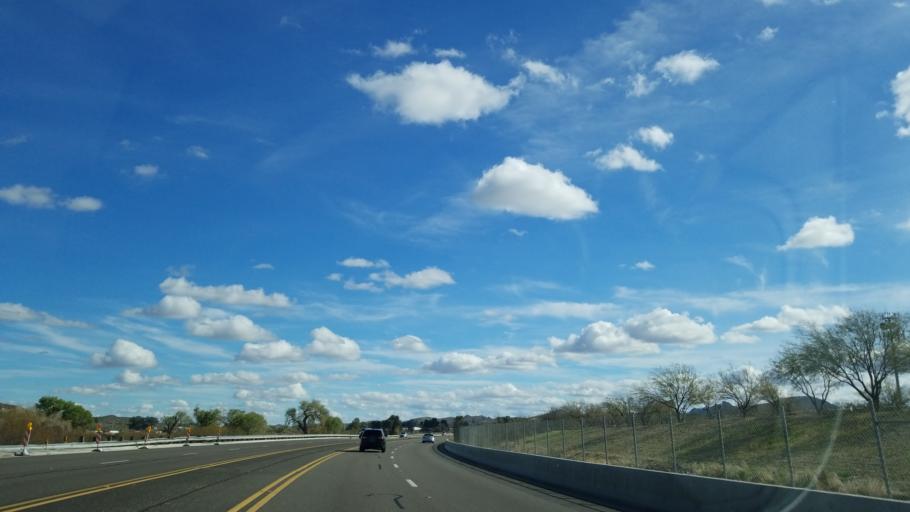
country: US
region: Arizona
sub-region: Maricopa County
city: Wickenburg
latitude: 33.9813
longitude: -112.7351
